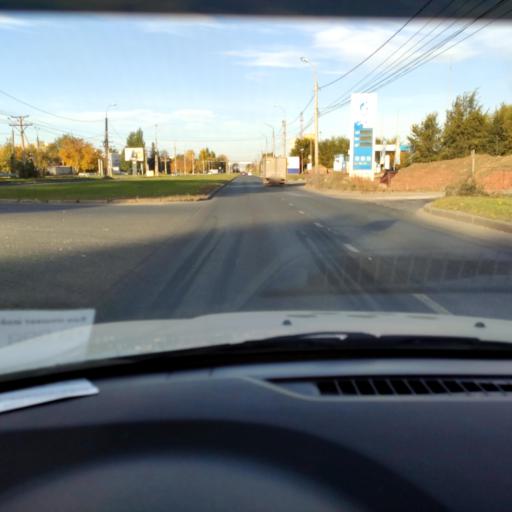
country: RU
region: Samara
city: Tol'yatti
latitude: 53.5597
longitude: 49.3068
